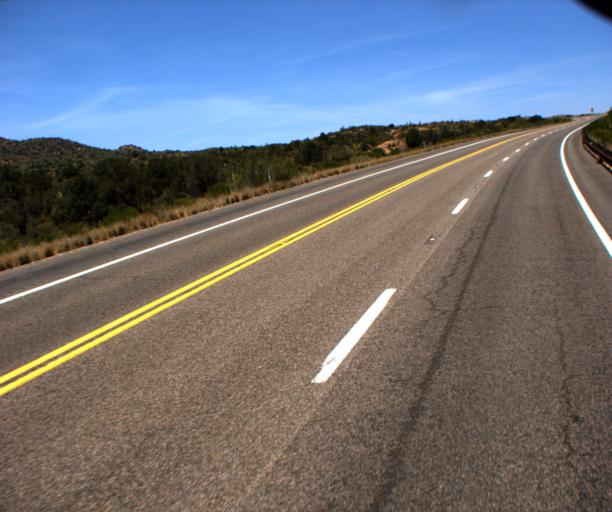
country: US
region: Arizona
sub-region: Gila County
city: Miami
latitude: 33.5275
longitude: -110.9138
